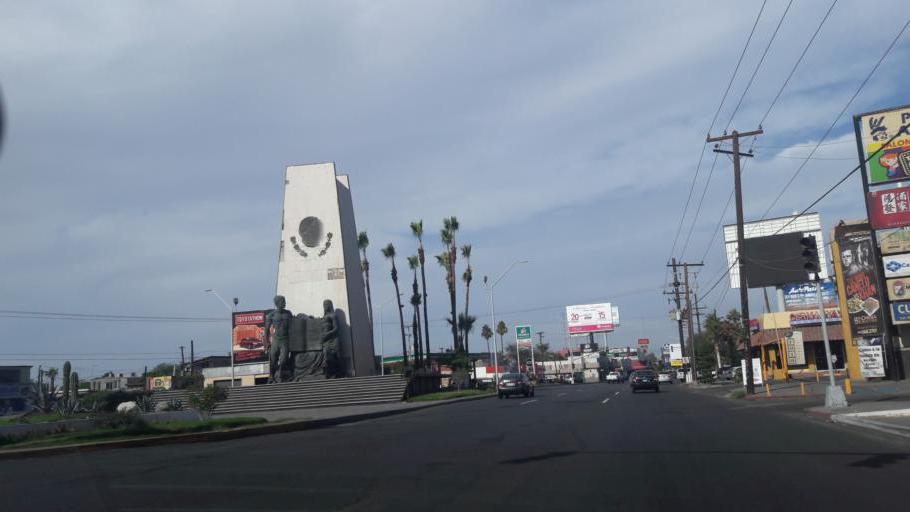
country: MX
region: Baja California
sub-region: Mexicali
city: Mexicali
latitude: 32.6474
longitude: -115.4519
